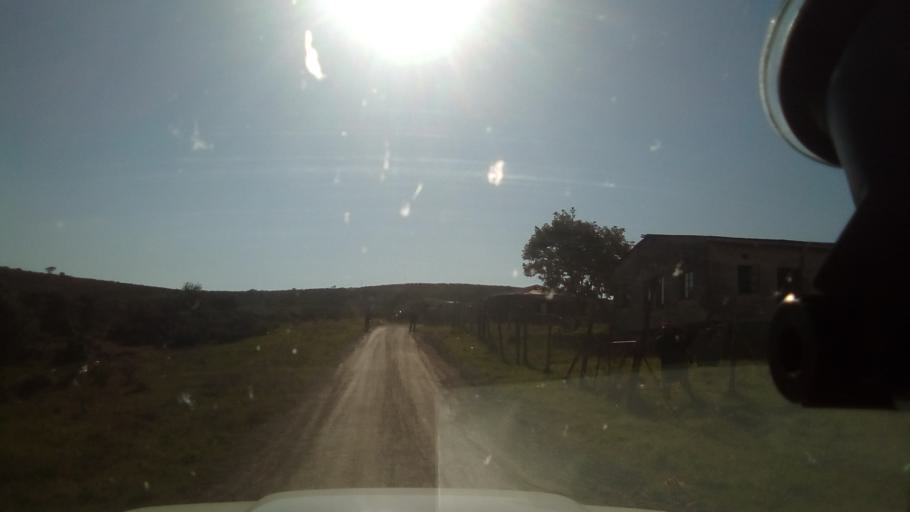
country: ZA
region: Eastern Cape
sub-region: Buffalo City Metropolitan Municipality
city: Bhisho
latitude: -32.8179
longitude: 27.3516
